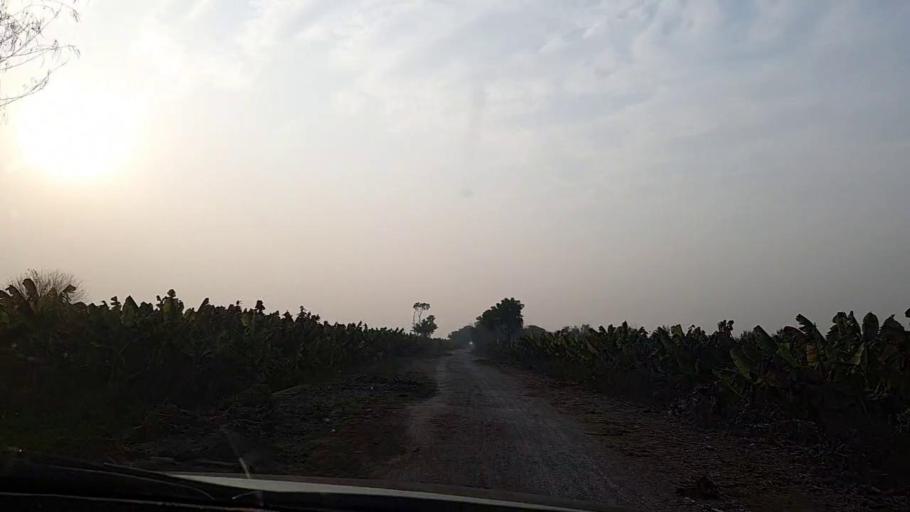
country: PK
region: Sindh
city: Nawabshah
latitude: 26.2943
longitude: 68.2821
